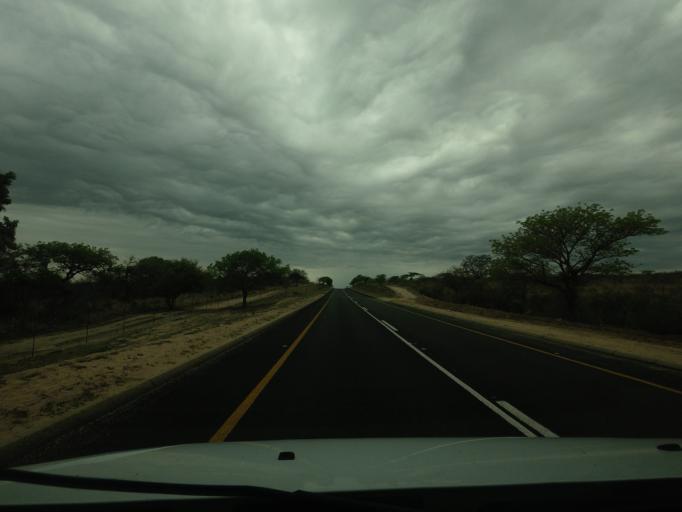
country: ZA
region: Limpopo
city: Thulamahashi
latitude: -24.5686
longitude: 31.0747
